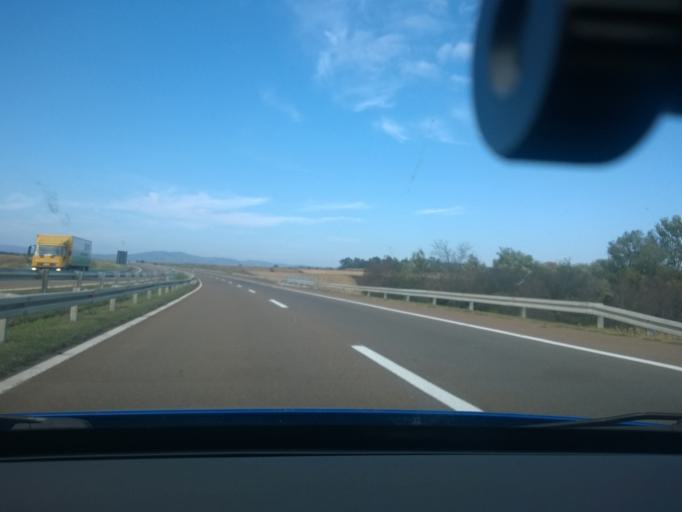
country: RS
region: Central Serbia
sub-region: Nisavski Okrug
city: Aleksinac
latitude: 43.5989
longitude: 21.6338
